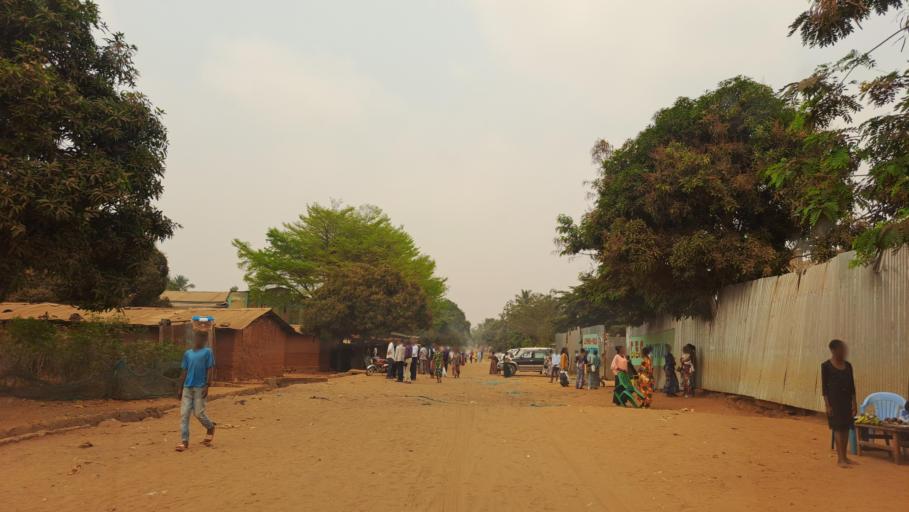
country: CD
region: Kasai-Oriental
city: Mbuji-Mayi
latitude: -6.1211
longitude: 23.6029
